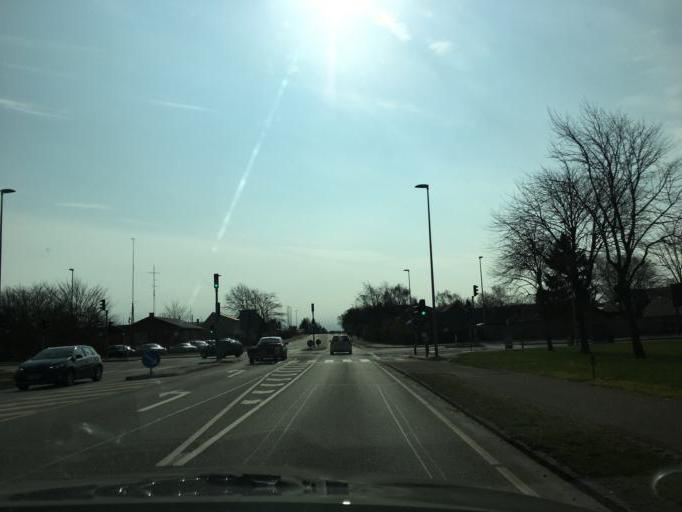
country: DK
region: South Denmark
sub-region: Vejen Kommune
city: Vejen
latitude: 55.4832
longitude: 9.1479
